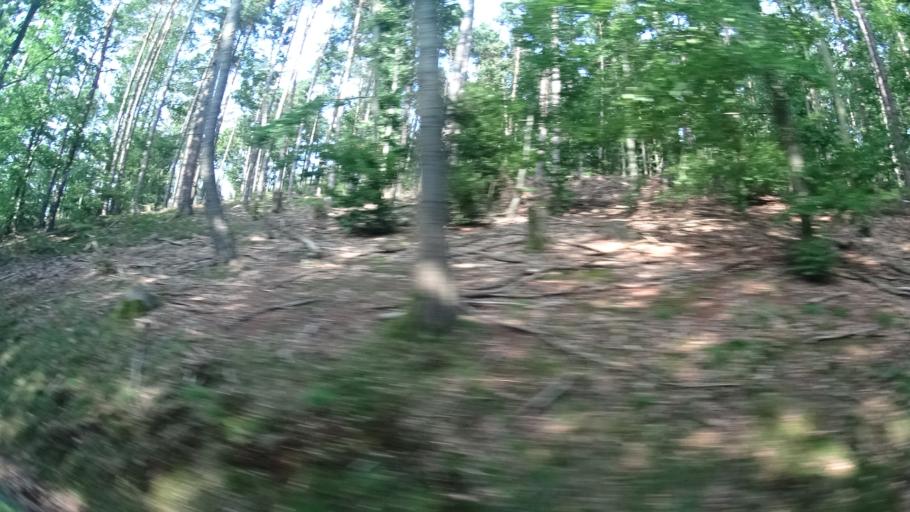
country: DE
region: Hesse
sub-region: Regierungsbezirk Darmstadt
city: Hesseneck
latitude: 49.5632
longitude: 9.0984
